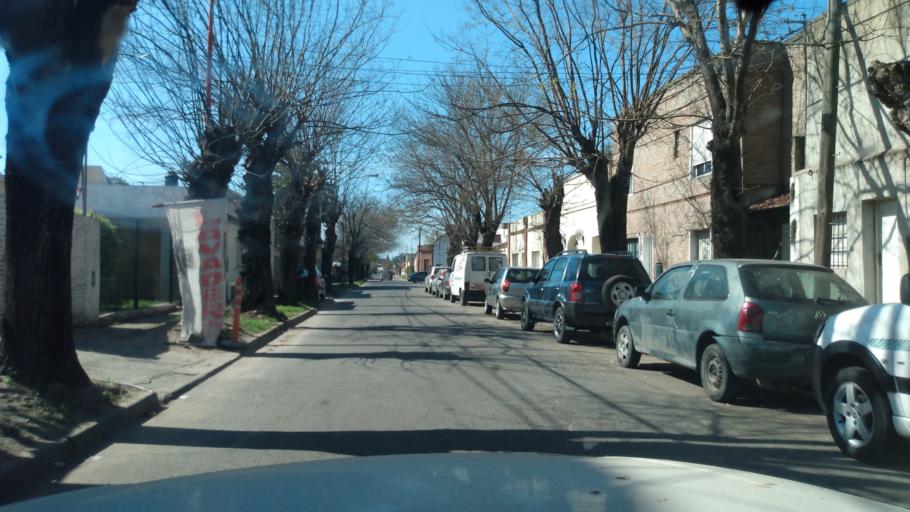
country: AR
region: Buenos Aires
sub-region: Partido de Lujan
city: Lujan
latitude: -34.5715
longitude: -59.1003
